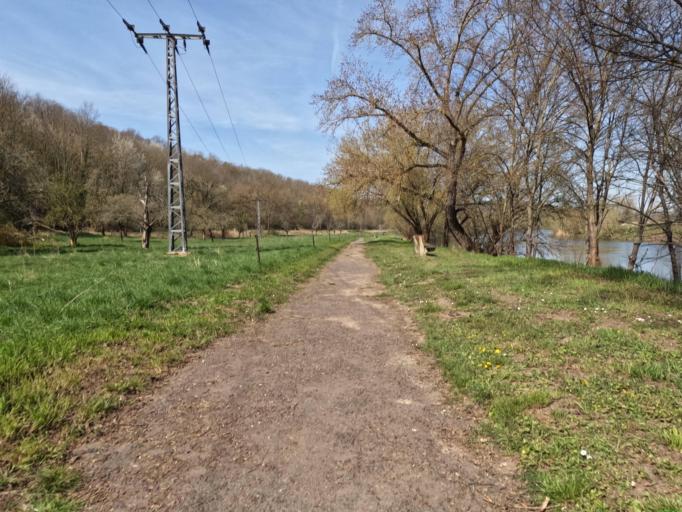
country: DE
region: Saxony-Anhalt
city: Beesenstedt
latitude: 51.5806
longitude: 11.7642
